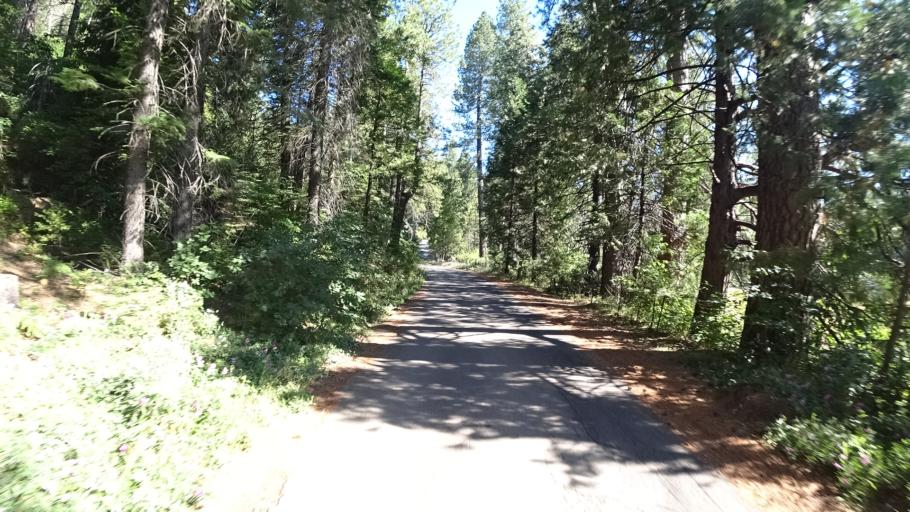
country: US
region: California
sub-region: Calaveras County
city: Arnold
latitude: 38.2639
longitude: -120.3444
